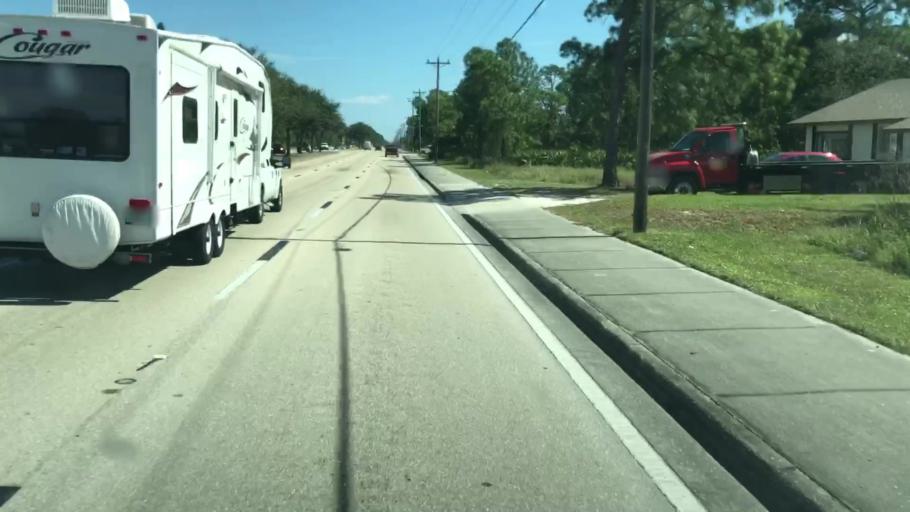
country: US
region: Florida
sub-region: Lee County
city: Gateway
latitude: 26.6169
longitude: -81.7069
